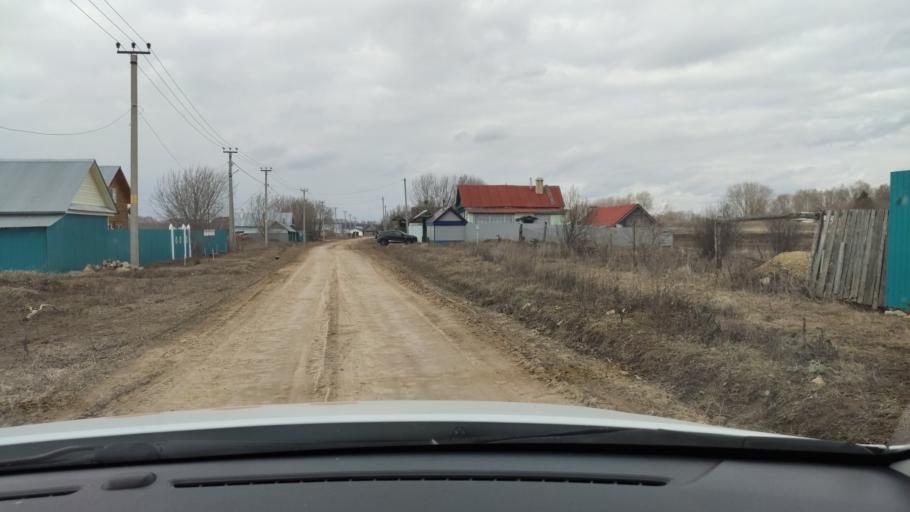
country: RU
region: Tatarstan
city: Vysokaya Gora
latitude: 56.2137
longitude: 49.3130
